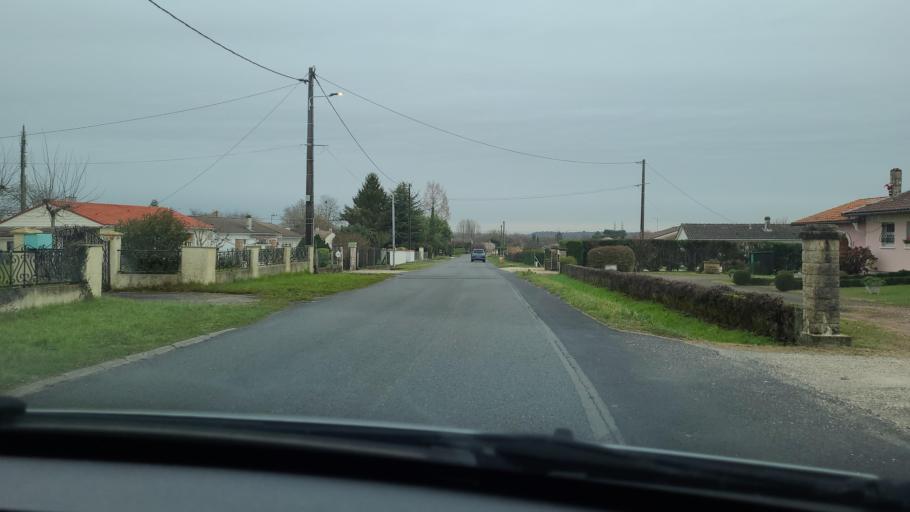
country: FR
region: Aquitaine
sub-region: Departement de la Gironde
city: Pugnac
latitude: 45.0826
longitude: -0.4890
